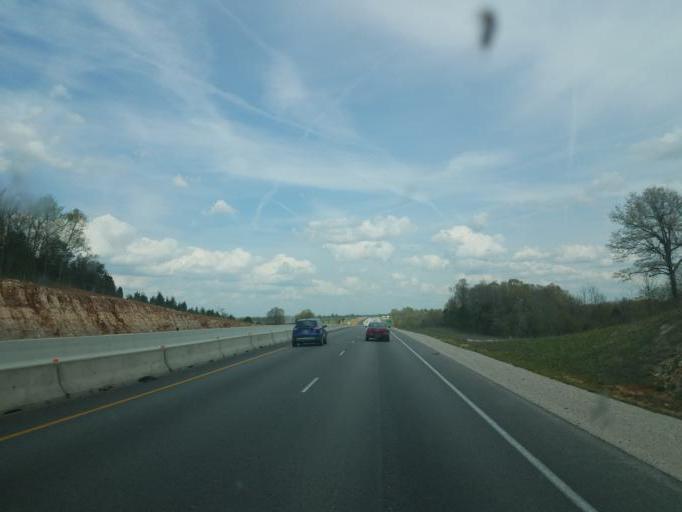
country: US
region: Kentucky
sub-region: Larue County
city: Hodgenville
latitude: 37.4705
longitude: -85.8818
